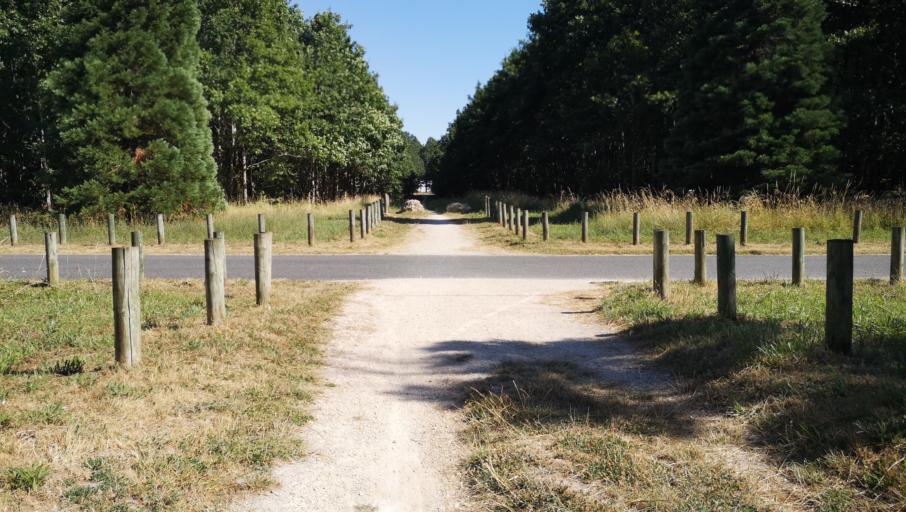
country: FR
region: Centre
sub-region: Departement du Loiret
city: Saint-Jean-de-Braye
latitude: 47.9312
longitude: 1.9849
